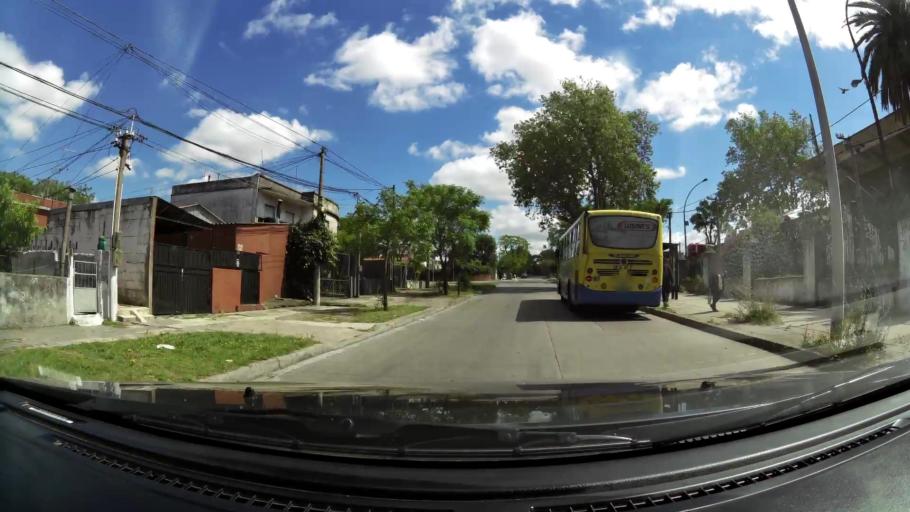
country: UY
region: Montevideo
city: Montevideo
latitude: -34.8570
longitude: -56.1439
